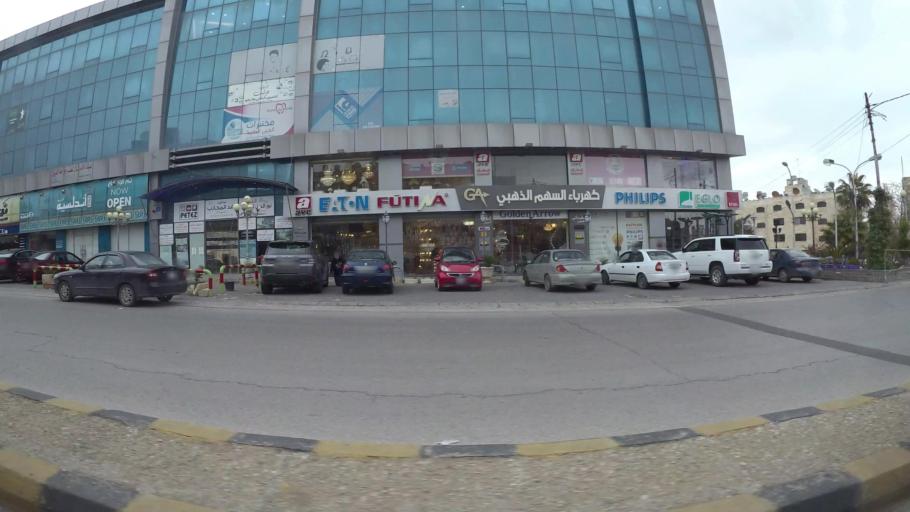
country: JO
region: Amman
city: Wadi as Sir
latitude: 31.9798
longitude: 35.8488
